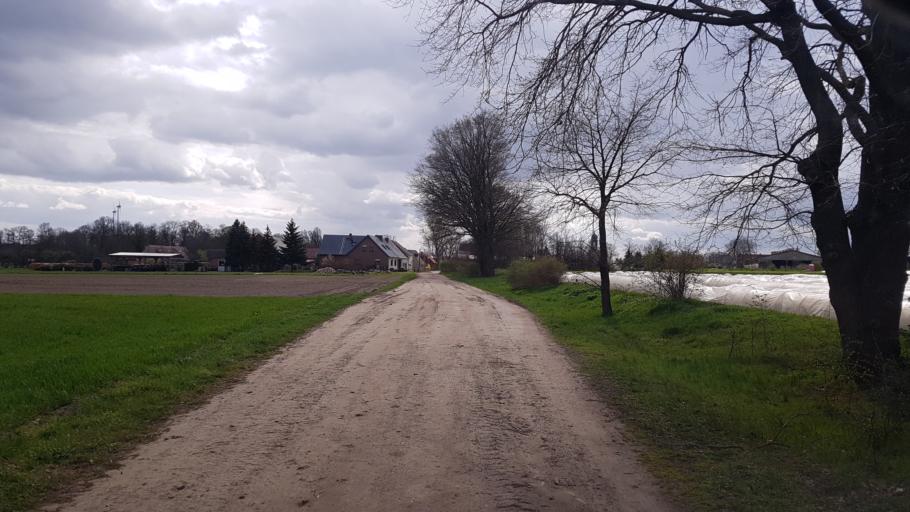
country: DE
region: Brandenburg
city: Calau
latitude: 51.7571
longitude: 14.0114
